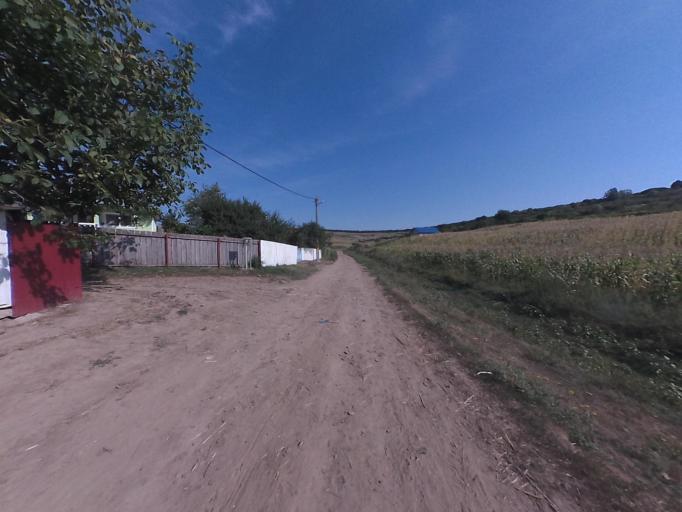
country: RO
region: Vaslui
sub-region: Comuna Osesti
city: Buda
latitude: 46.7686
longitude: 27.4304
